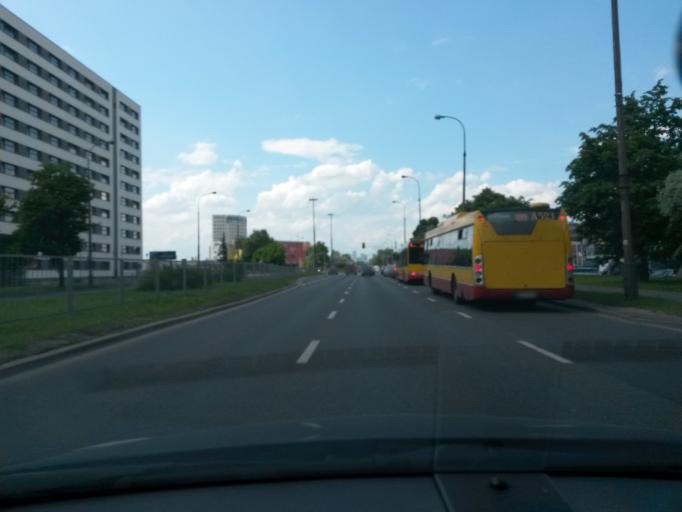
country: PL
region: Masovian Voivodeship
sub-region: Warszawa
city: Mokotow
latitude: 52.1869
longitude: 21.0505
